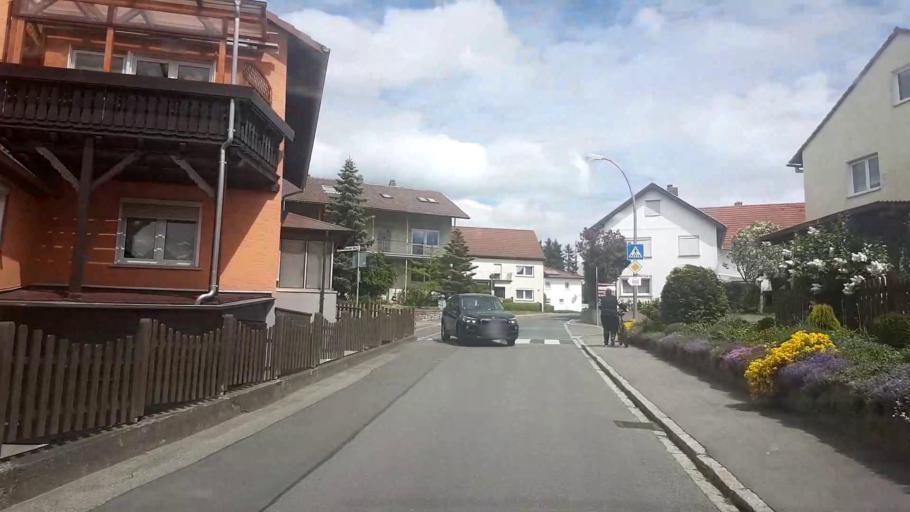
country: DE
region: Bavaria
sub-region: Upper Franconia
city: Untersiemau
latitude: 50.1951
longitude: 10.9737
